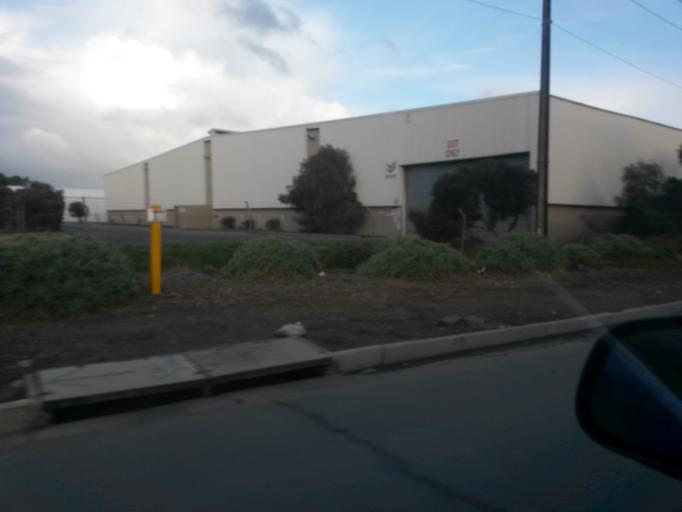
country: AU
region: South Australia
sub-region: Port Adelaide Enfield
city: Birkenhead
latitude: -34.8413
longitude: 138.5149
